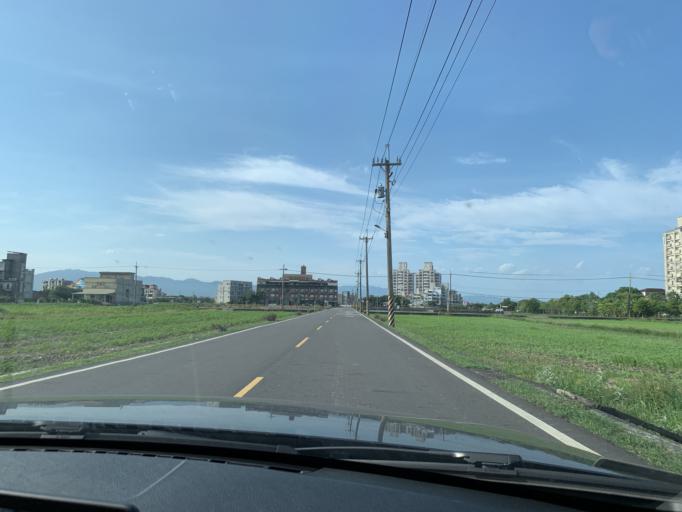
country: TW
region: Taiwan
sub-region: Yilan
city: Yilan
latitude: 24.6757
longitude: 121.8101
